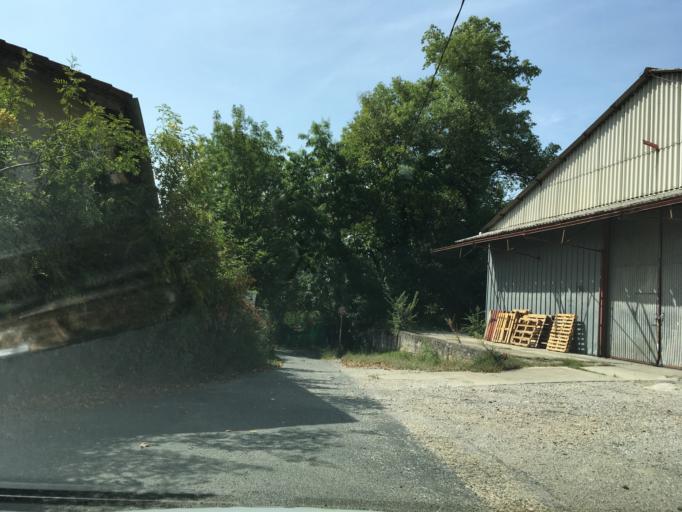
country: FR
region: Midi-Pyrenees
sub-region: Departement du Tarn
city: Castres
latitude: 43.6147
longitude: 2.2661
